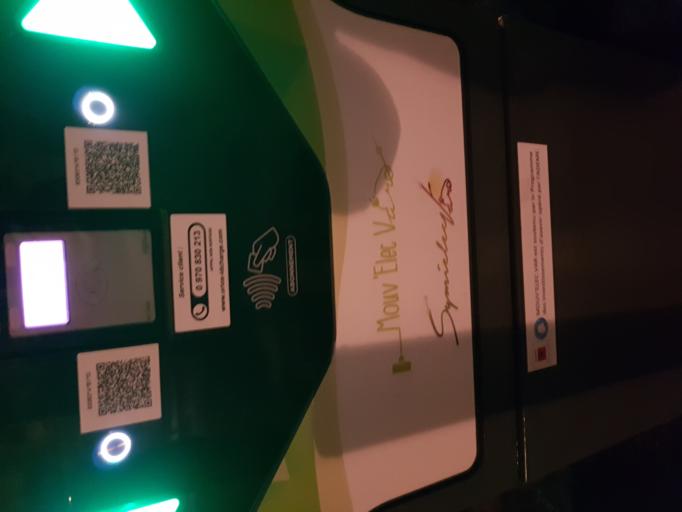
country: FR
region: Provence-Alpes-Cote d'Azur
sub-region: Departement du Var
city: La Garde-Freinet
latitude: 43.3178
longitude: 6.4693
